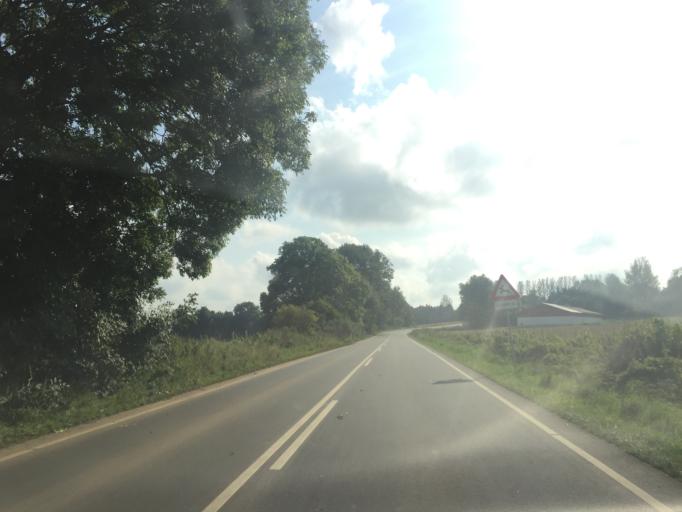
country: DK
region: Zealand
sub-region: Holbaek Kommune
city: Tollose
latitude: 55.6290
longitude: 11.7892
